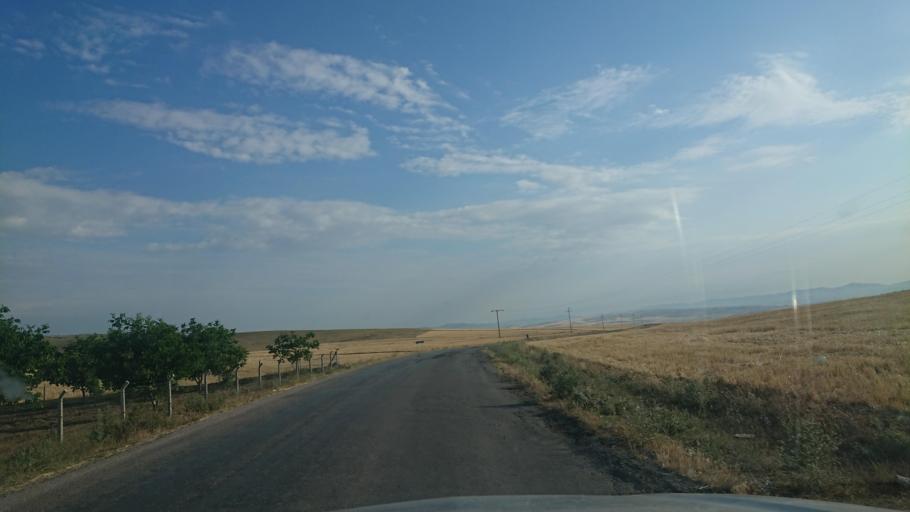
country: TR
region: Aksaray
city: Ortakoy
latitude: 38.7776
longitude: 34.0607
